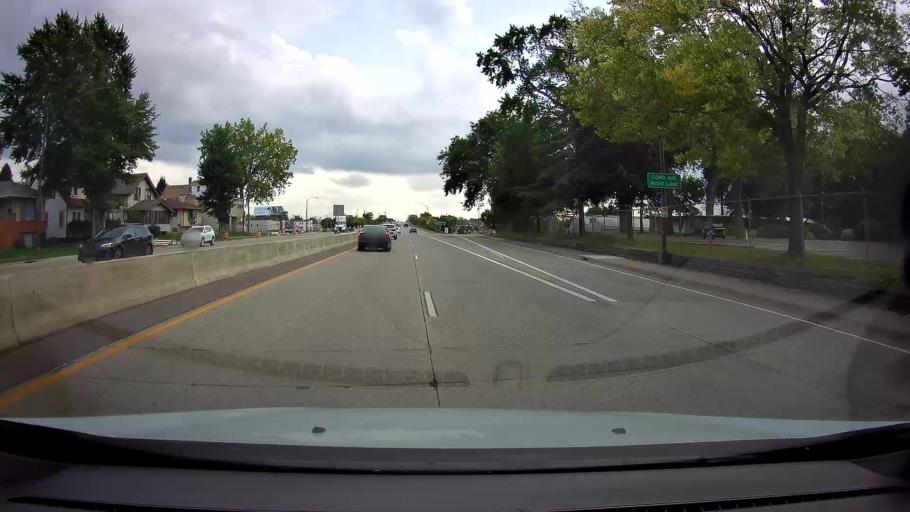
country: US
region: Minnesota
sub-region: Ramsey County
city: Falcon Heights
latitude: 44.9801
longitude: -93.1671
